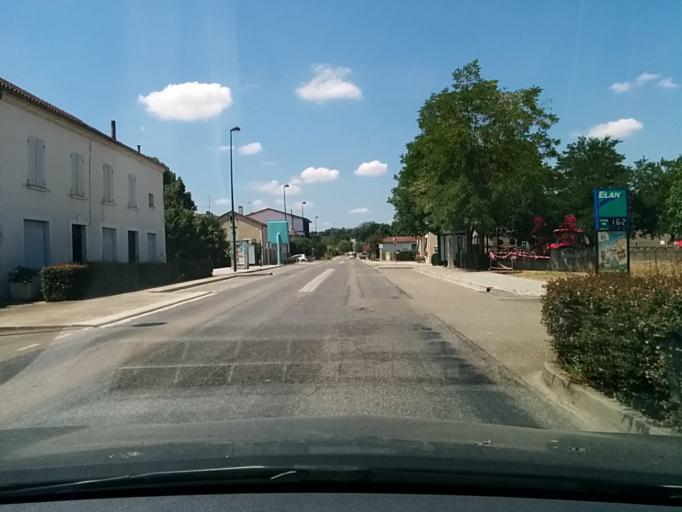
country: FR
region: Midi-Pyrenees
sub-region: Departement du Gers
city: Vic-Fezensac
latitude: 43.7242
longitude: 0.3789
